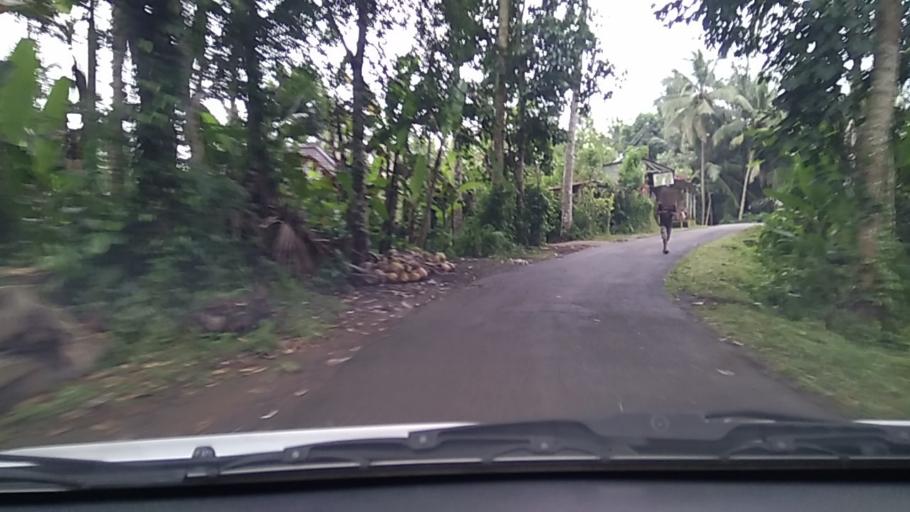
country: ID
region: Bali
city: Tegalalang
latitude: -8.4238
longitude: 115.2799
